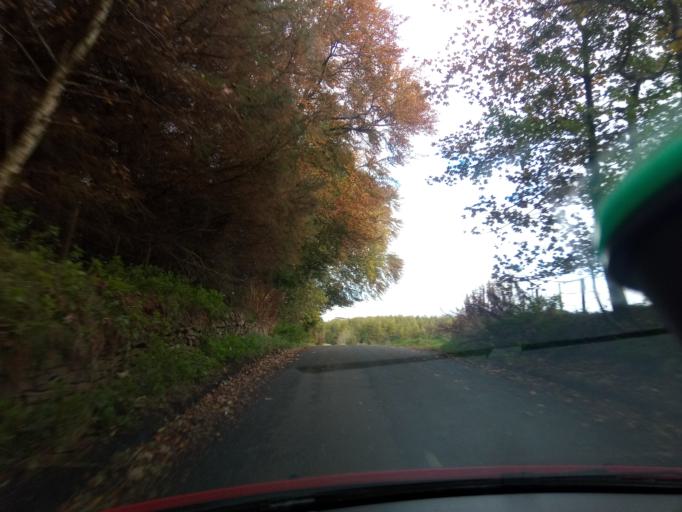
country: GB
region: Scotland
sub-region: South Lanarkshire
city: Carnwath
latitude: 55.7376
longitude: -3.6041
